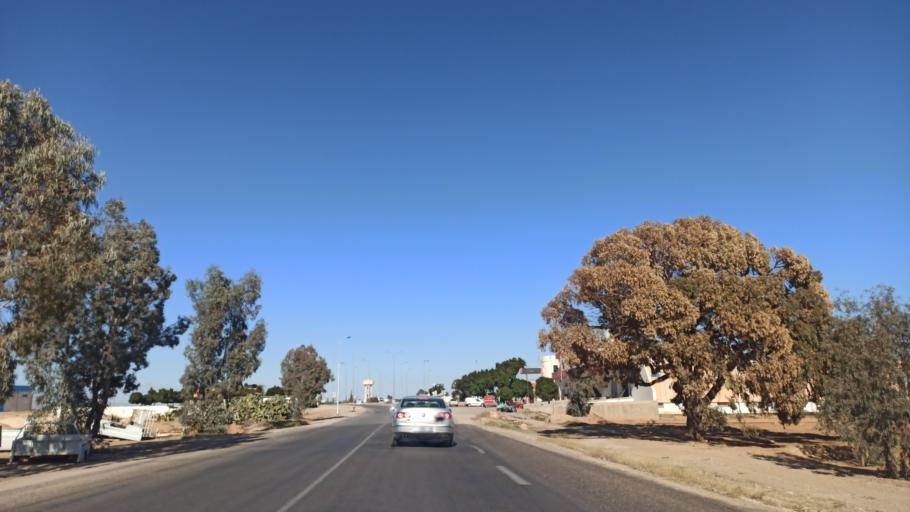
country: TN
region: Sidi Bu Zayd
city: Jilma
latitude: 35.1451
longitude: 9.3627
